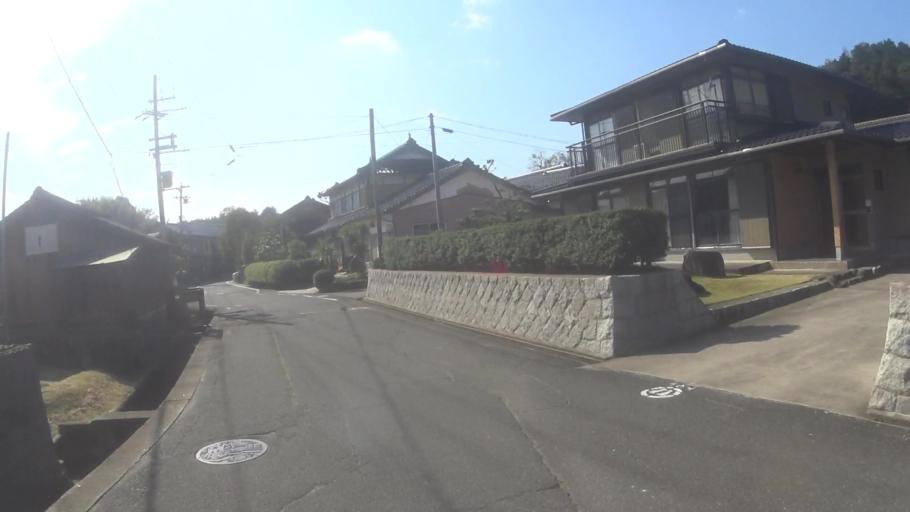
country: JP
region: Kyoto
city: Miyazu
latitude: 35.6711
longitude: 135.0730
